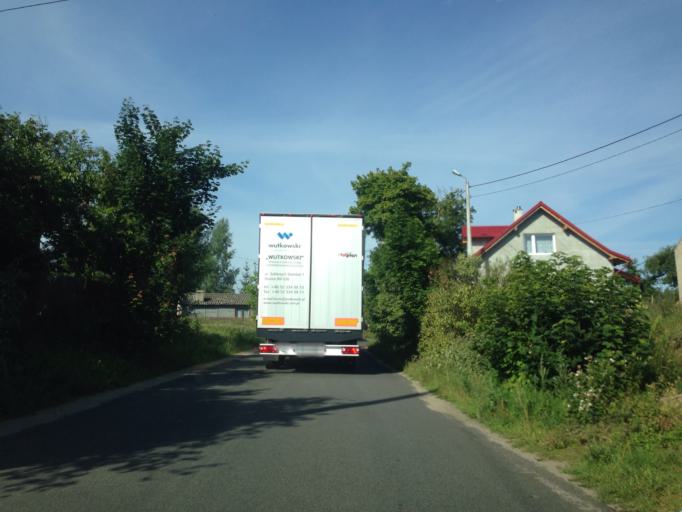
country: PL
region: Pomeranian Voivodeship
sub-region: Powiat starogardzki
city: Osiek
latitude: 53.7399
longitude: 18.4365
